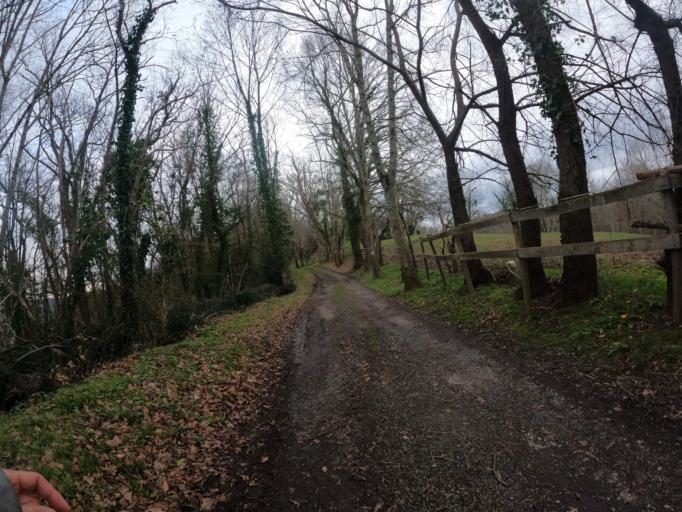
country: FR
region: Aquitaine
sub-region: Departement des Pyrenees-Atlantiques
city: Mazeres-Lezons
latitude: 43.2708
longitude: -0.3562
